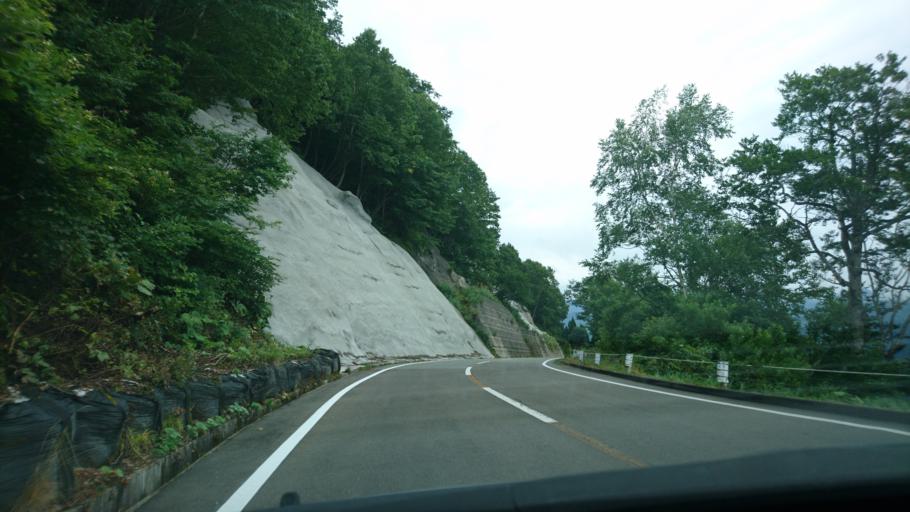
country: JP
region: Akita
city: Yuzawa
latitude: 38.9801
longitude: 140.7212
